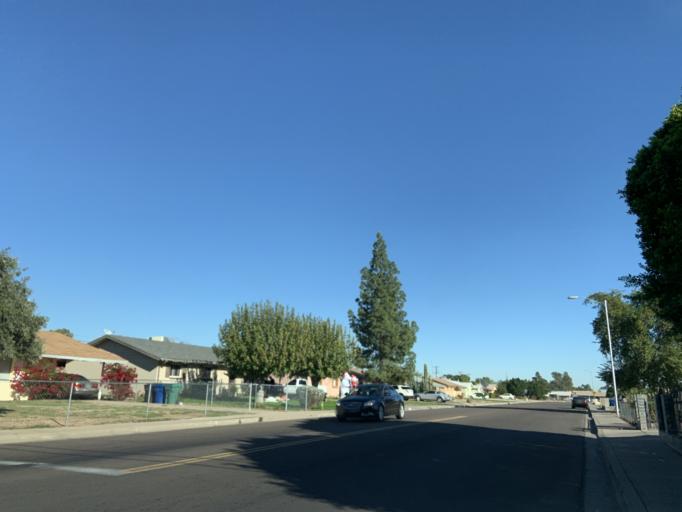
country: US
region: Arizona
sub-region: Maricopa County
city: Mesa
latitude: 33.4007
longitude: -111.8617
